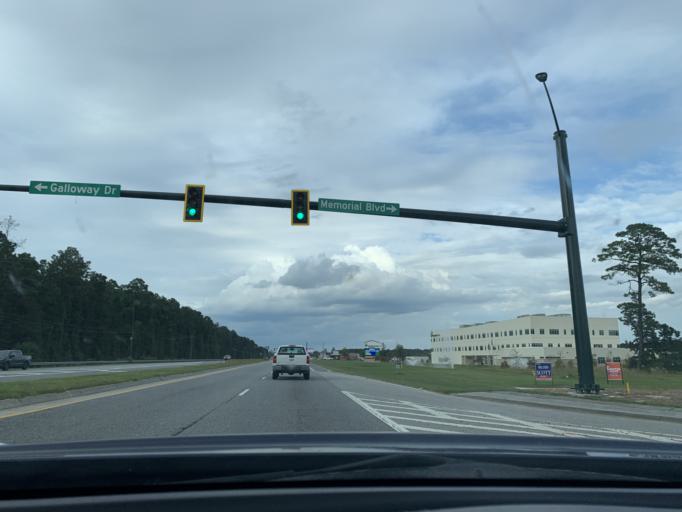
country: US
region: Georgia
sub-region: Chatham County
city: Pooler
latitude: 32.0883
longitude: -81.2772
